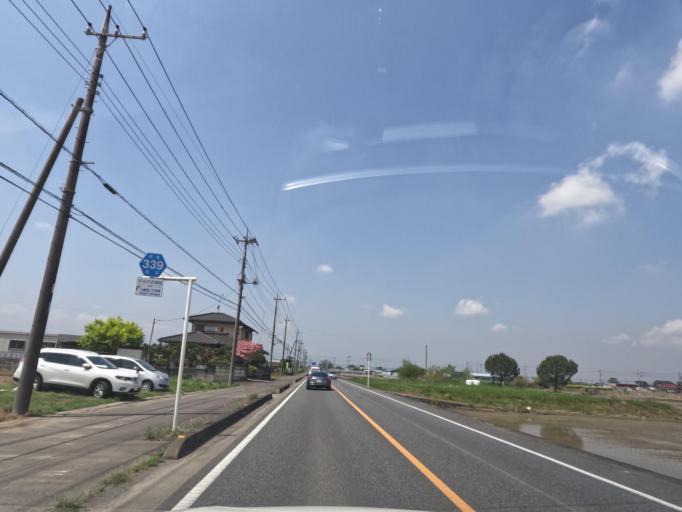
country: JP
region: Saitama
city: Kawagoe
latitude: 35.9635
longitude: 139.4967
